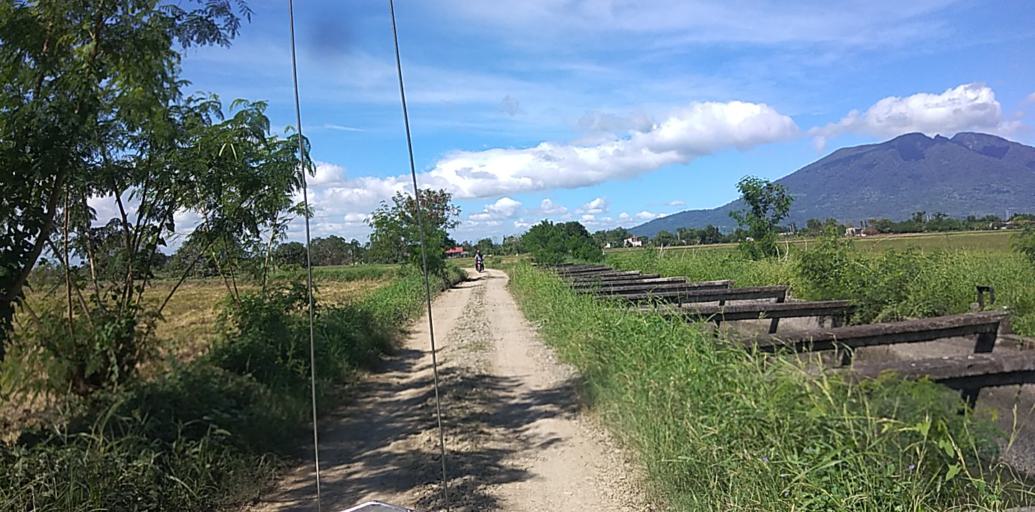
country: PH
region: Central Luzon
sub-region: Province of Pampanga
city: Candating
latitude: 15.1308
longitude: 120.7961
